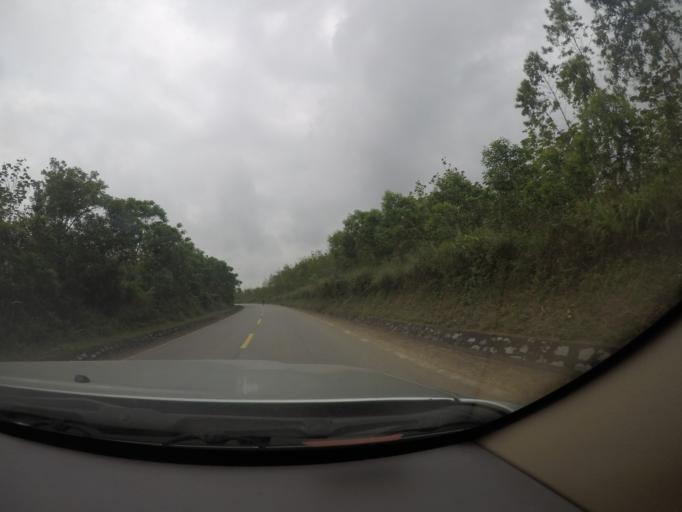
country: VN
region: Quang Binh
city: Hoan Lao
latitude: 17.5630
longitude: 106.4437
